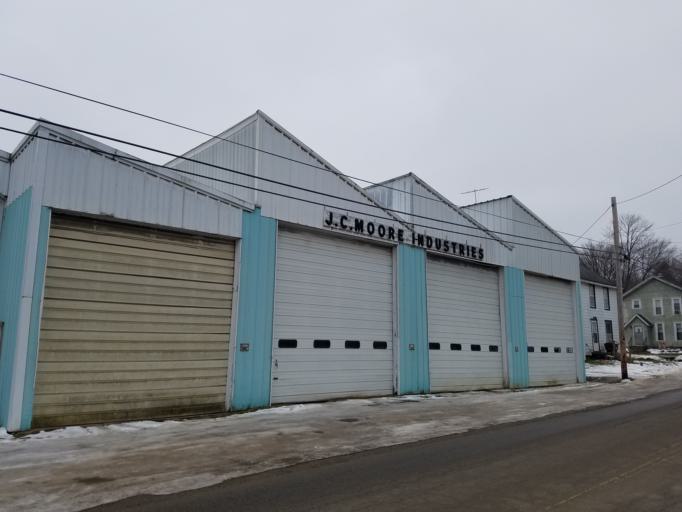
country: US
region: Pennsylvania
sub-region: Mercer County
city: Mercer
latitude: 41.3221
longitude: -80.2598
